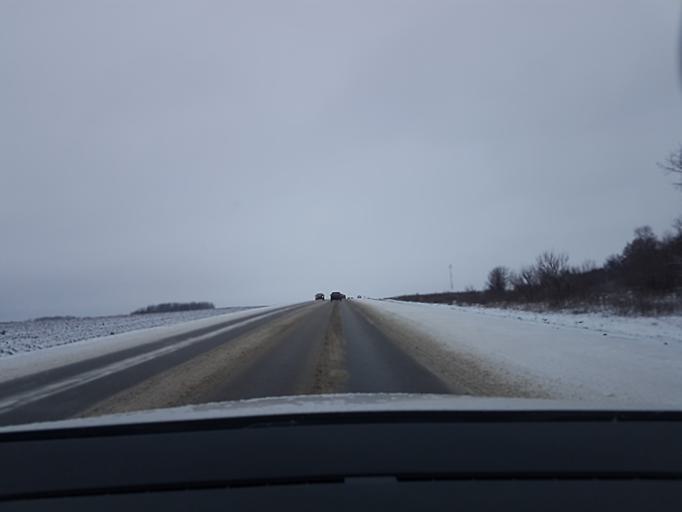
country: RU
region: Rjazan
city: Pavelets
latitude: 53.9916
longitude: 39.3532
